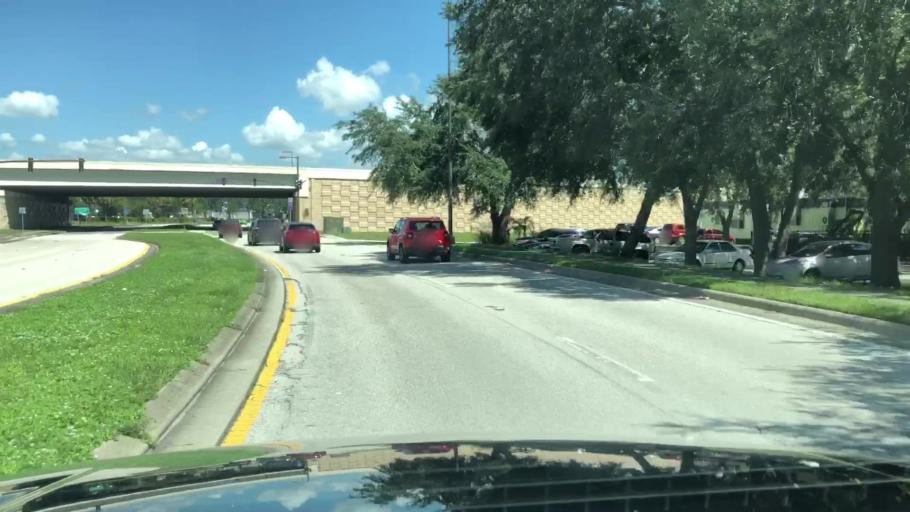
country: US
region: Florida
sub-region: Osceola County
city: Celebration
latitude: 28.3391
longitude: -81.4855
